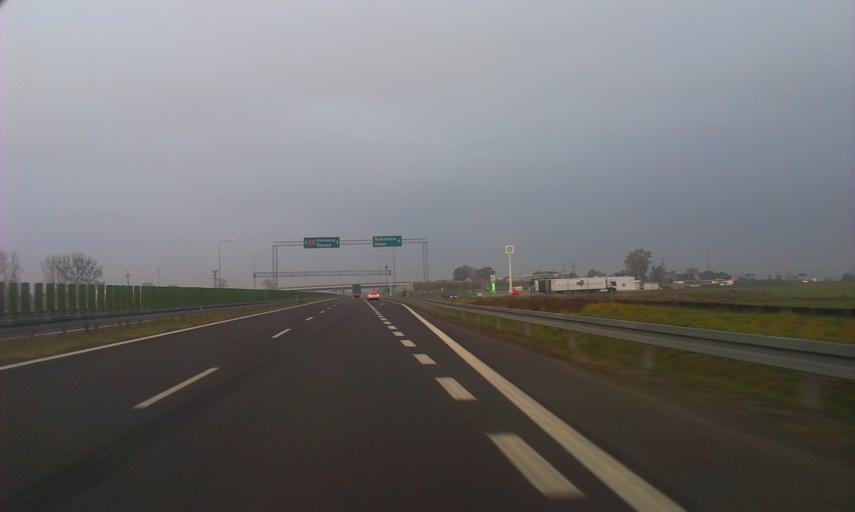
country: PL
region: Greater Poland Voivodeship
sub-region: Powiat poznanski
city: Rokietnica
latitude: 52.4986
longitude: 16.7588
